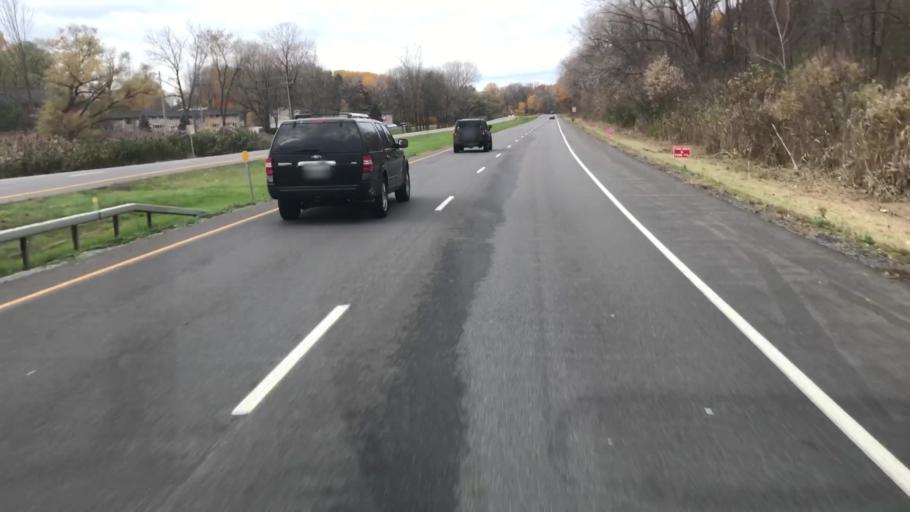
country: US
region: New York
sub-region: Onondaga County
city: Liverpool
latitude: 43.1311
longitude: -76.2224
